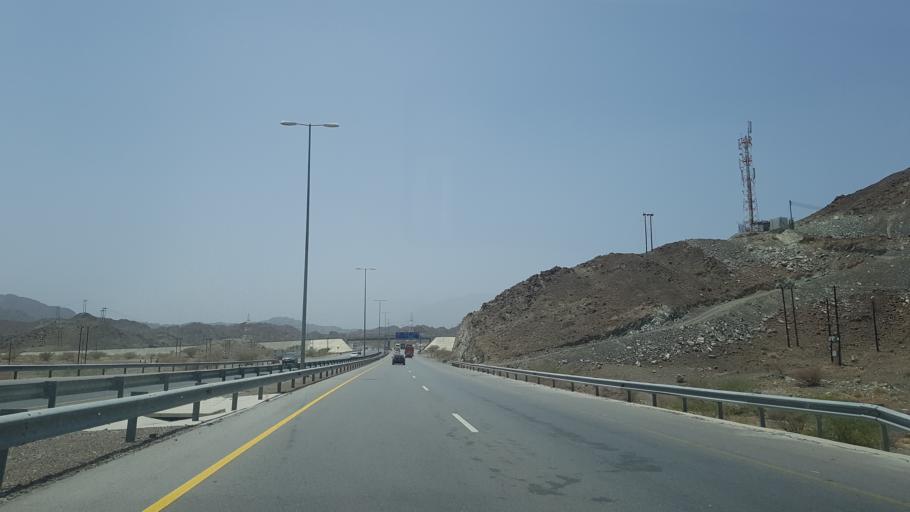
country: OM
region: Muhafazat ad Dakhiliyah
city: Sufalat Sama'il
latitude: 23.3724
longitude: 58.0468
